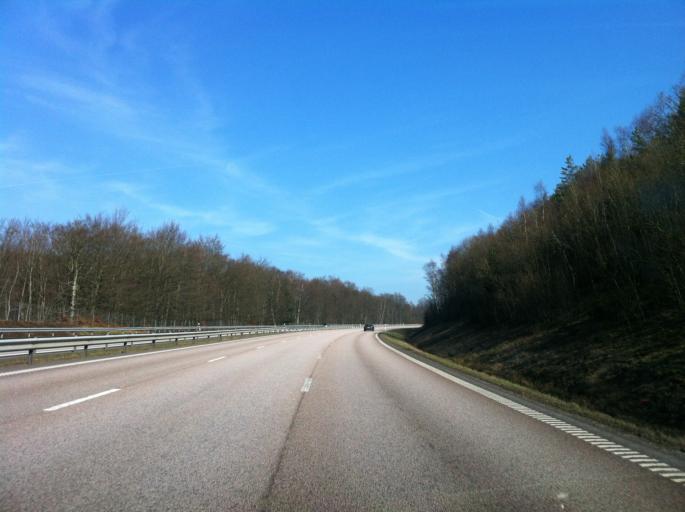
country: SE
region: Skane
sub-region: Bastads Kommun
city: Forslov
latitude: 56.3462
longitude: 12.9202
